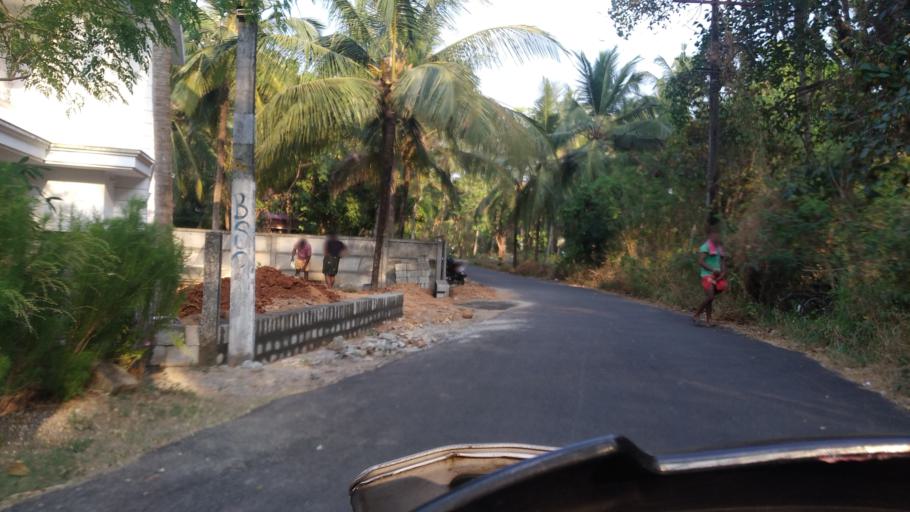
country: IN
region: Kerala
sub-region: Thrissur District
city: Thanniyam
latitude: 10.4390
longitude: 76.0799
